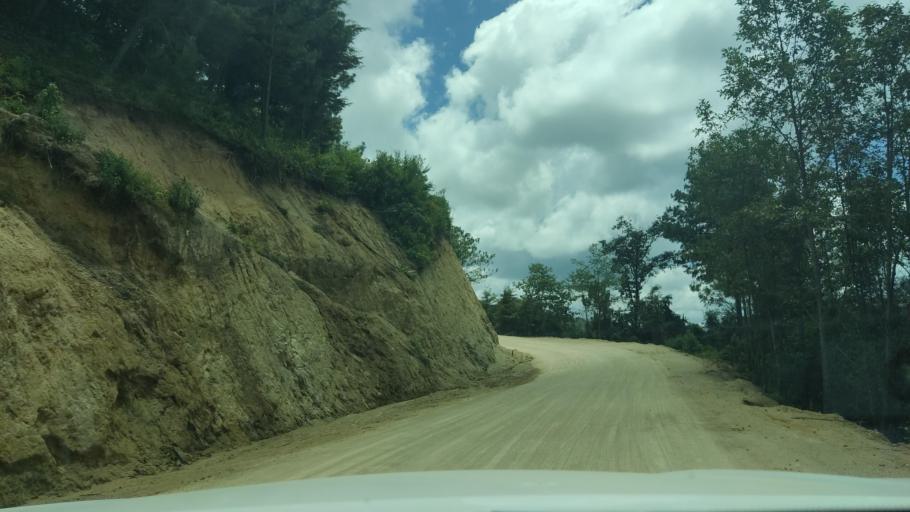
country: GT
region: Chimaltenango
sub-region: Municipio de San Juan Comalapa
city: Comalapa
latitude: 14.7806
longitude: -90.8682
